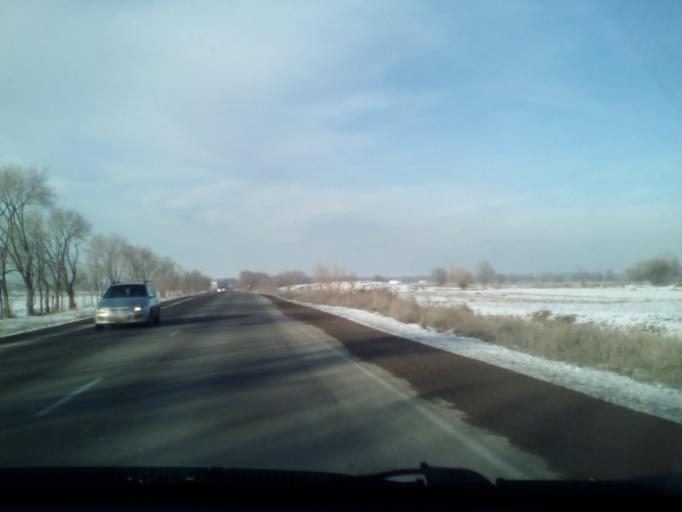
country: KZ
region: Almaty Oblysy
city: Burunday
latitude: 43.2072
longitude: 76.4150
